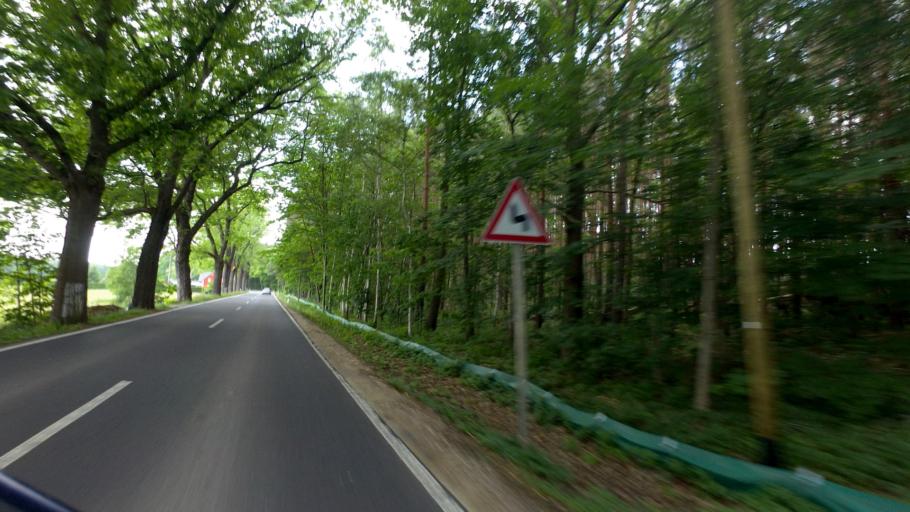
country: DE
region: Saxony
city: Quitzdorf
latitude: 51.3060
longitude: 14.7617
